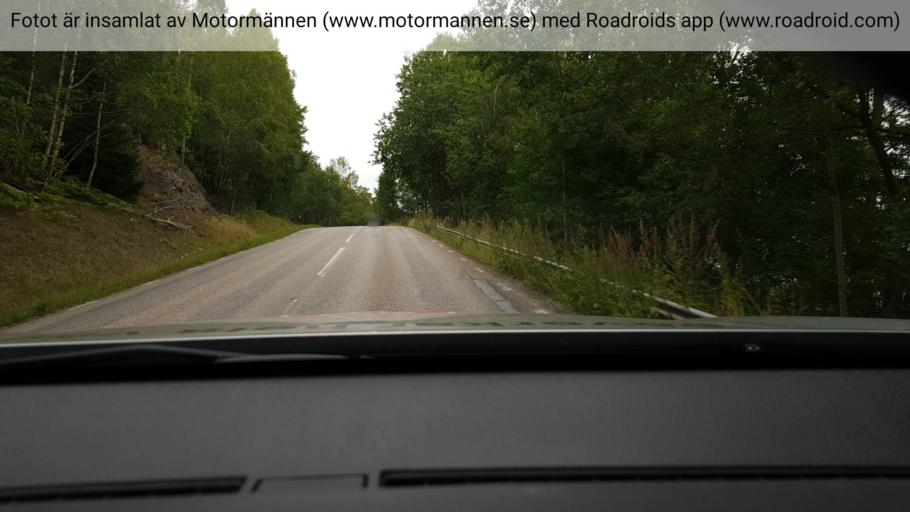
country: SE
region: Soedermanland
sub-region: Gnesta Kommun
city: Gnesta
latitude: 59.0253
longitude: 17.3359
